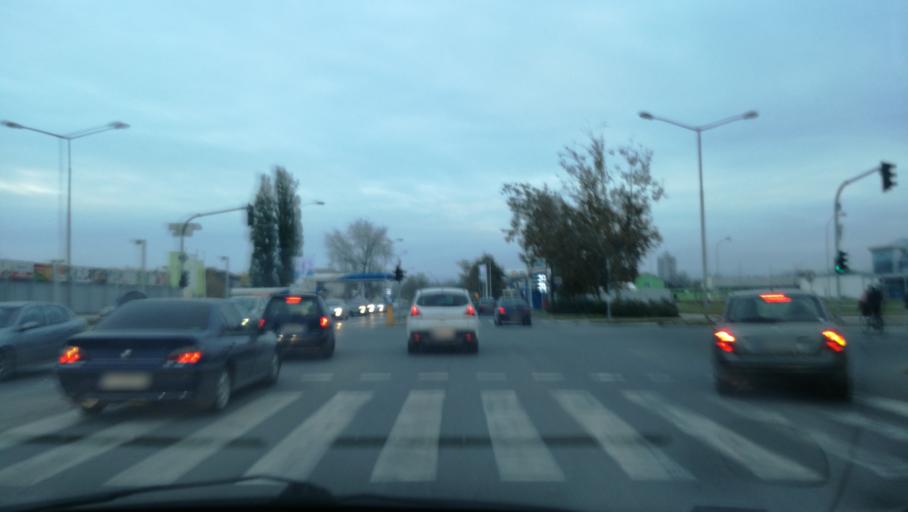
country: RS
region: Autonomna Pokrajina Vojvodina
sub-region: Juznobacki Okrug
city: Novi Sad
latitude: 45.2735
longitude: 19.8302
